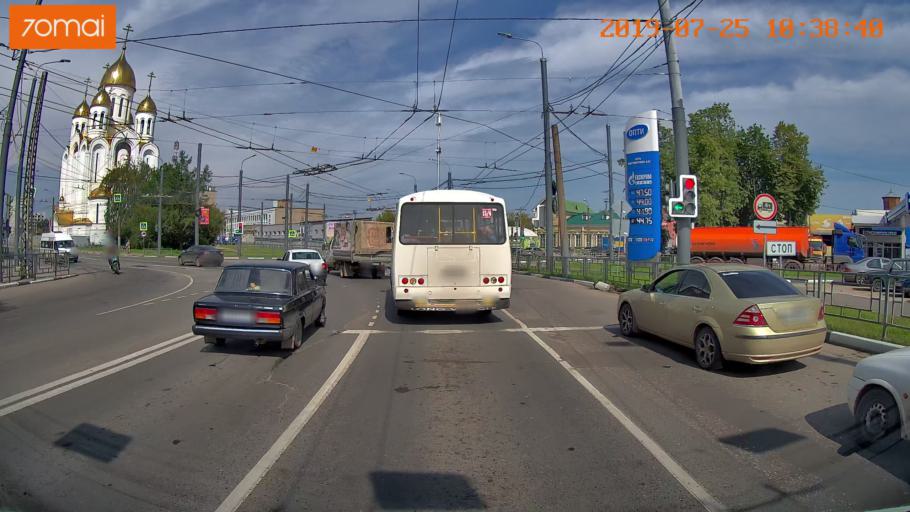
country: RU
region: Ivanovo
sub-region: Gorod Ivanovo
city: Ivanovo
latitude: 57.0159
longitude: 40.9841
